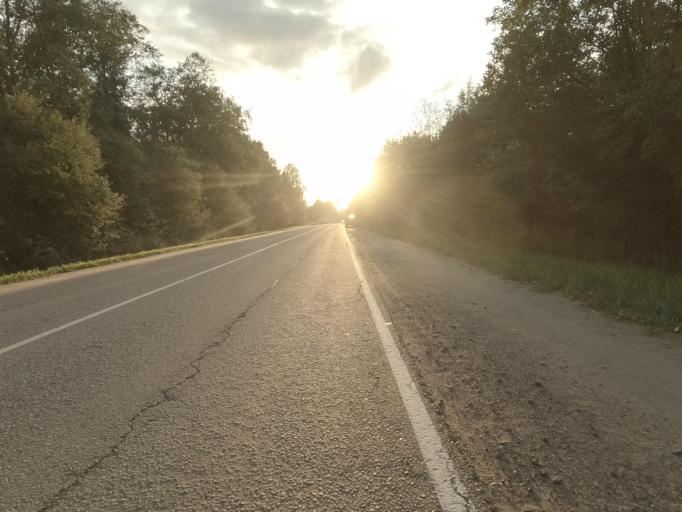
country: RU
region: Leningrad
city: Mga
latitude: 59.7626
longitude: 30.9901
